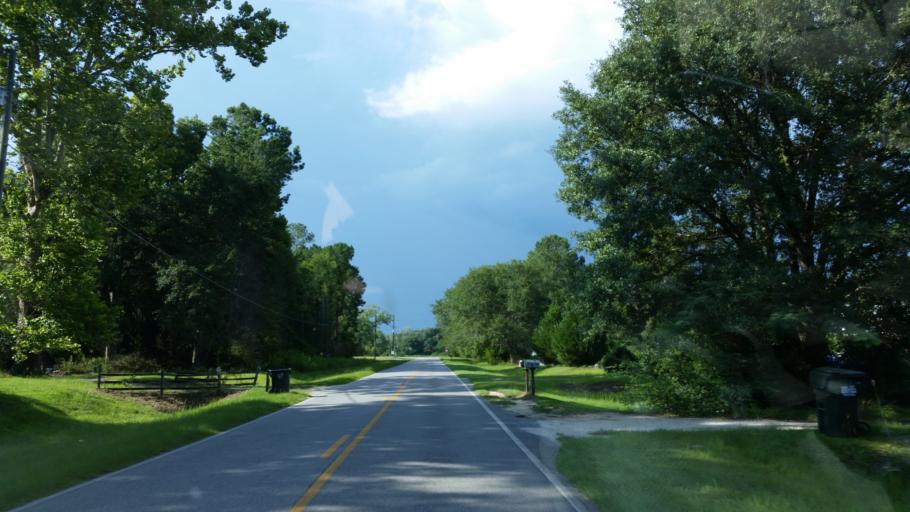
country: US
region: Georgia
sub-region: Lowndes County
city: Hahira
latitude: 30.9821
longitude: -83.3951
